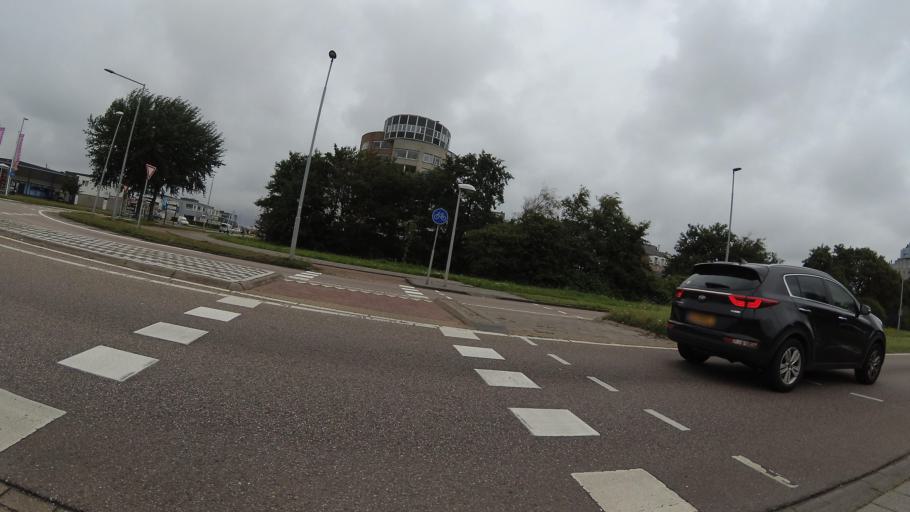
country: NL
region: North Holland
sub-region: Gemeente Den Helder
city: Den Helder
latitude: 52.9428
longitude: 4.7777
